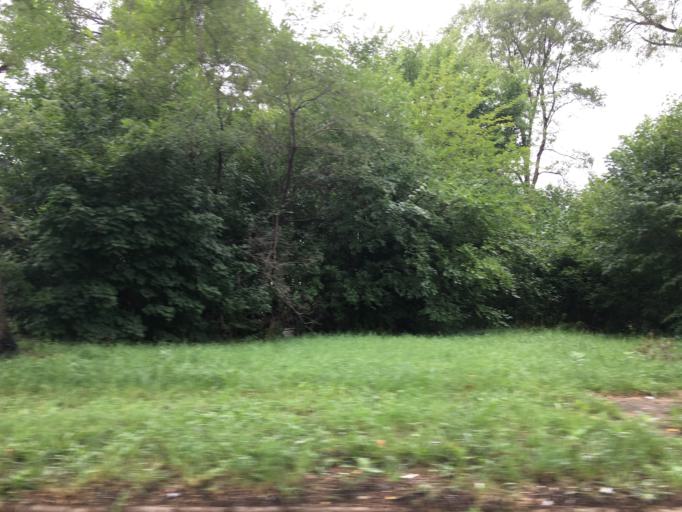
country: US
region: Michigan
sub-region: Wayne County
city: Highland Park
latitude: 42.4129
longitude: -83.1450
